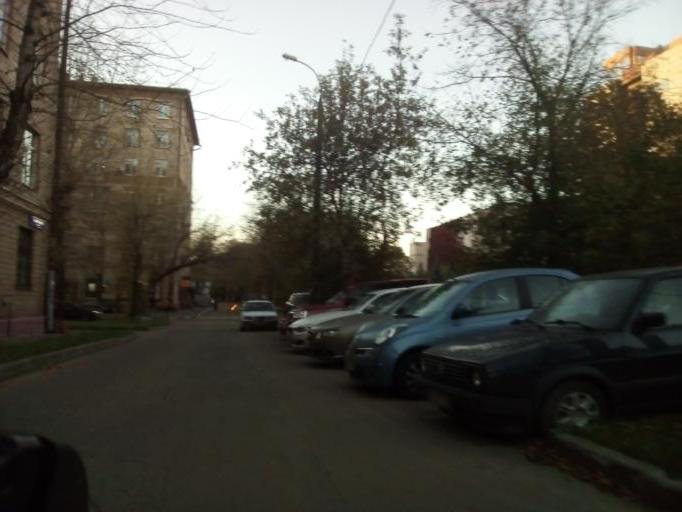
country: RU
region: Moscow
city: Sokol
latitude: 55.8035
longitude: 37.4974
